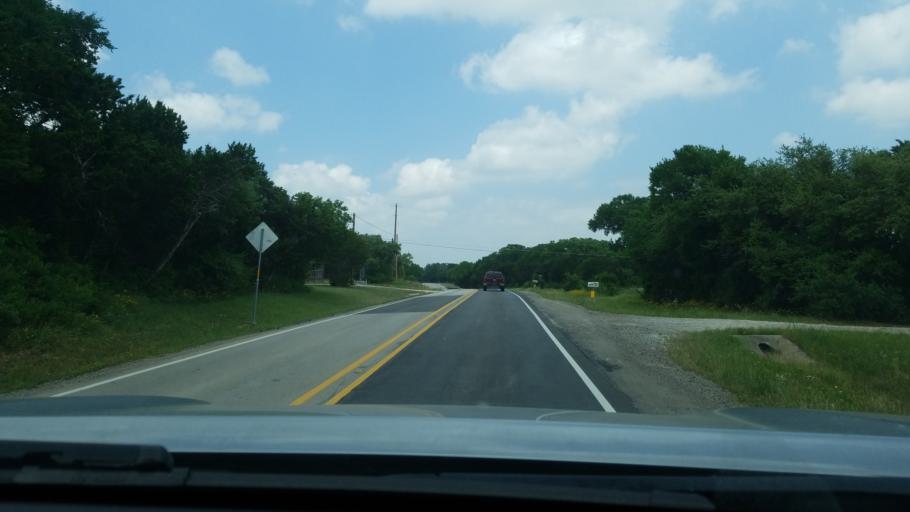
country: US
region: Texas
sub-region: Hays County
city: Dripping Springs
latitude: 30.1376
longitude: -98.0323
